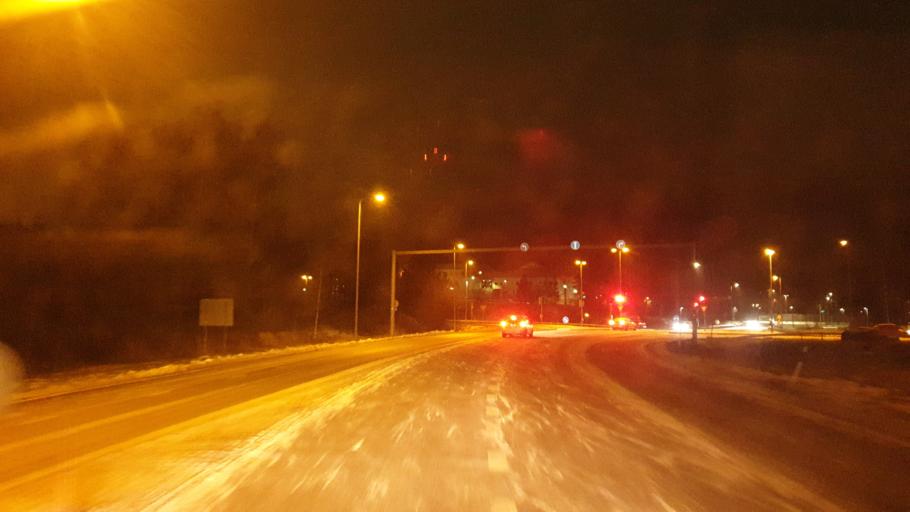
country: FI
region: Southern Savonia
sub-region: Savonlinna
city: Savonlinna
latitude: 61.8661
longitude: 28.9403
